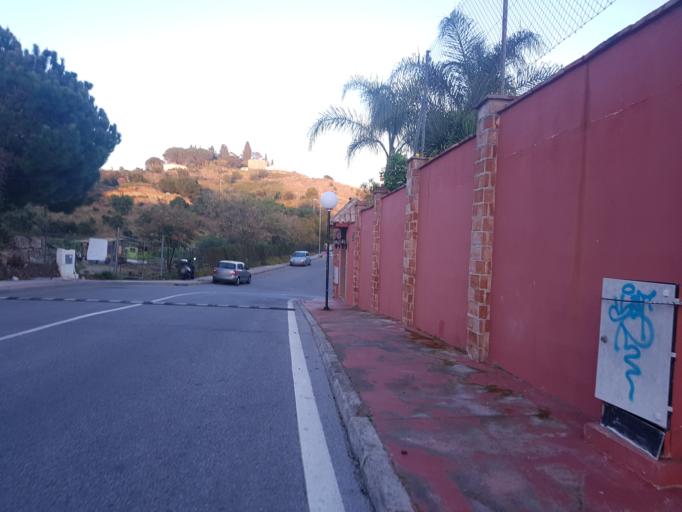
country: ES
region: Andalusia
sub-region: Provincia de Malaga
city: Marbella
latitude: 36.5226
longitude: -4.8891
